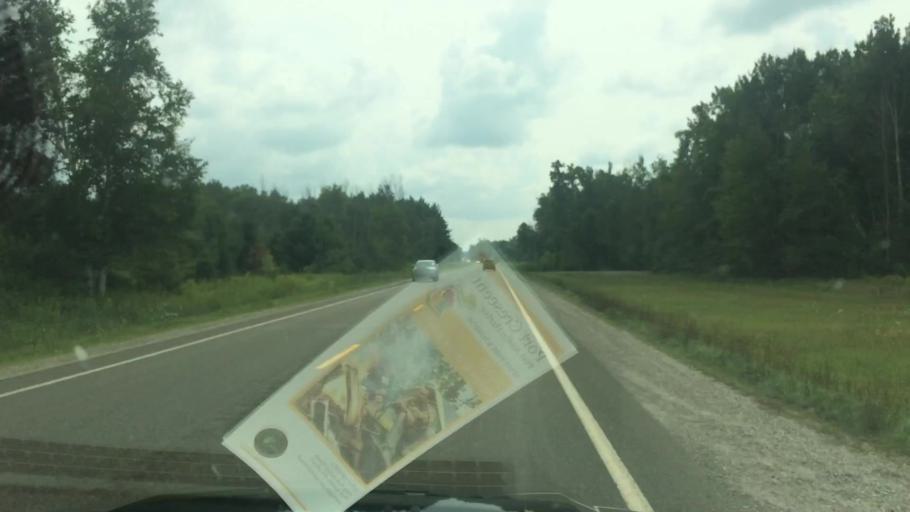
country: US
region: Michigan
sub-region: Tuscola County
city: Cass City
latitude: 43.6519
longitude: -83.0983
